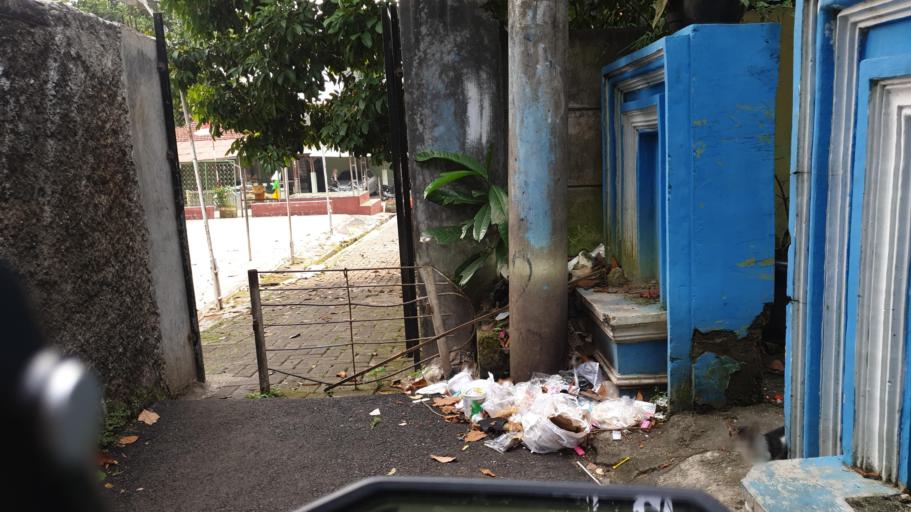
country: ID
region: West Java
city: Depok
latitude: -6.3439
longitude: 106.8315
